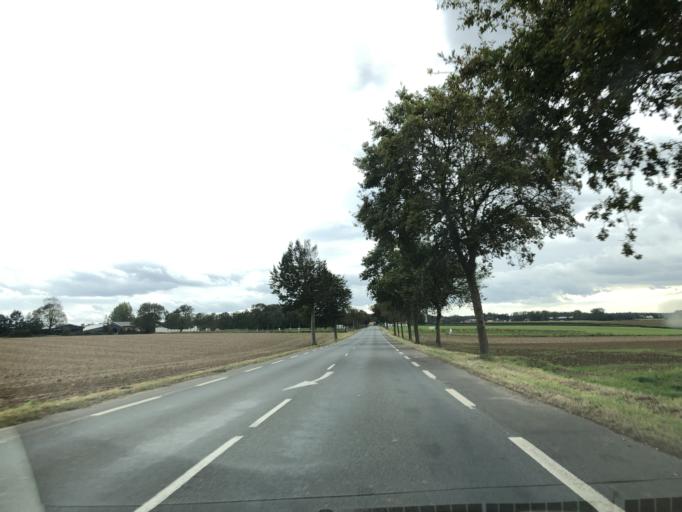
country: FR
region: Nord-Pas-de-Calais
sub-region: Departement du Pas-de-Calais
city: Marconne
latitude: 50.4204
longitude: 2.0550
